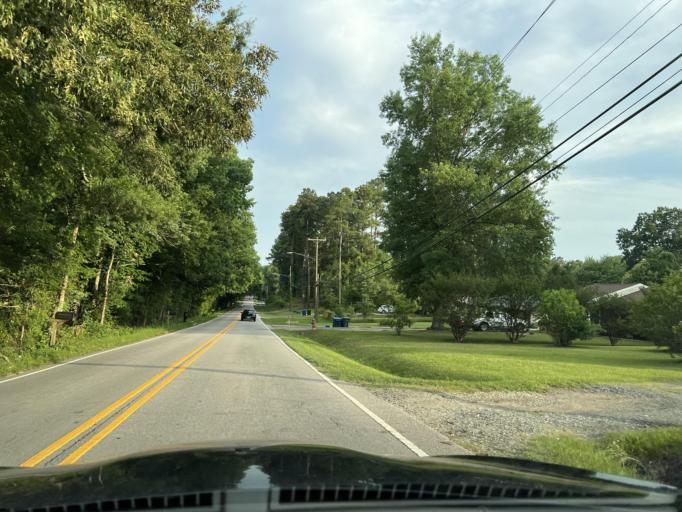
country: US
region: North Carolina
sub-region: Durham County
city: Gorman
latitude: 35.9848
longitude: -78.8430
